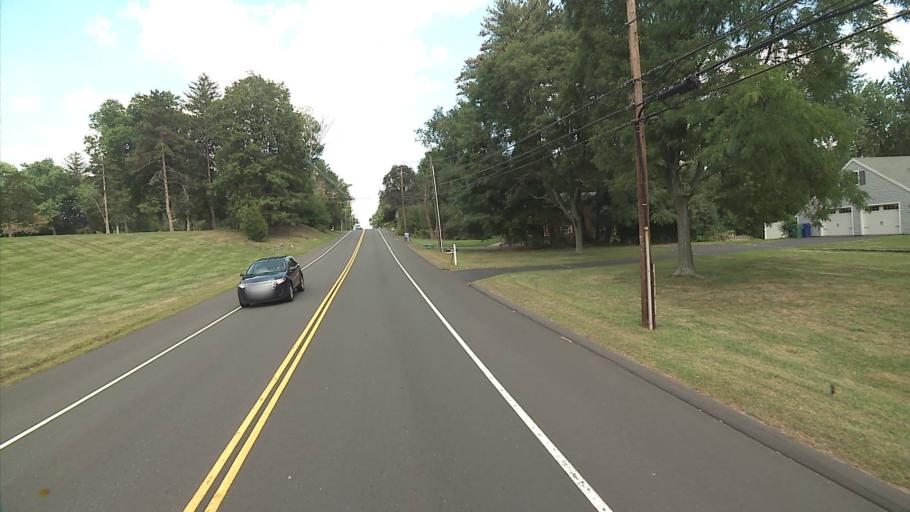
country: US
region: Connecticut
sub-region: Hartford County
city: Blue Hills
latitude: 41.8079
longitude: -72.7307
